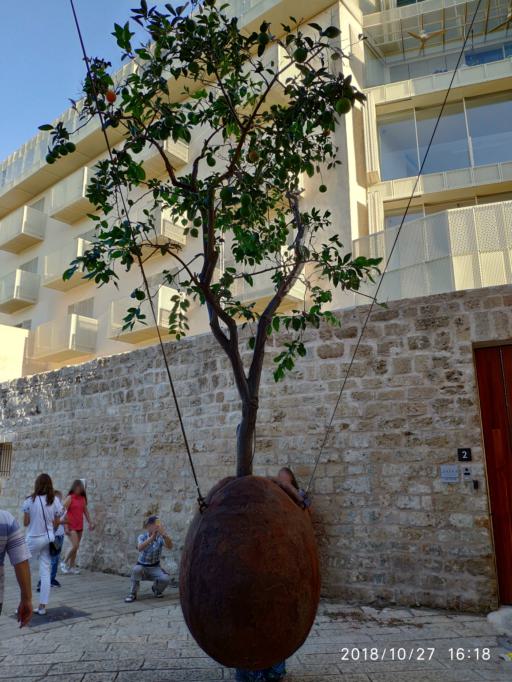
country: IL
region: Tel Aviv
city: Yafo
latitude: 32.0531
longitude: 34.7527
